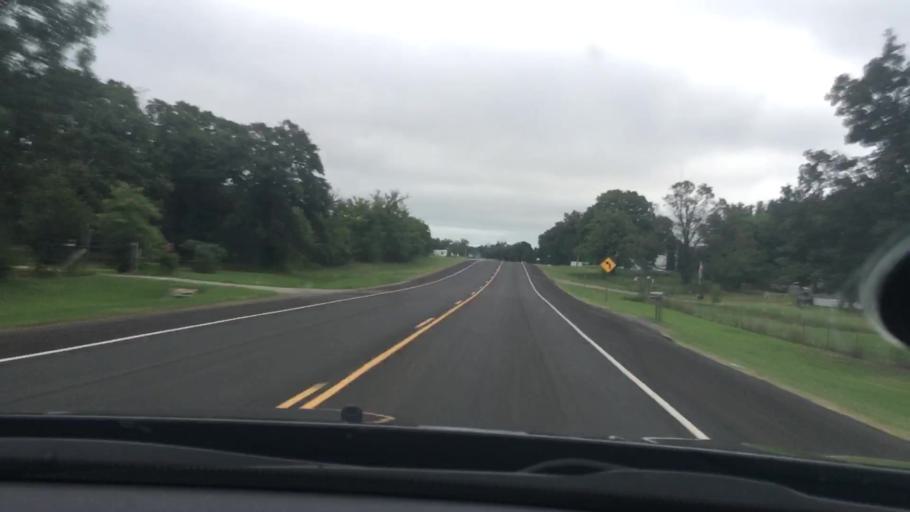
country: US
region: Oklahoma
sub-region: Sequoyah County
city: Vian
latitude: 35.5604
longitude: -94.9812
